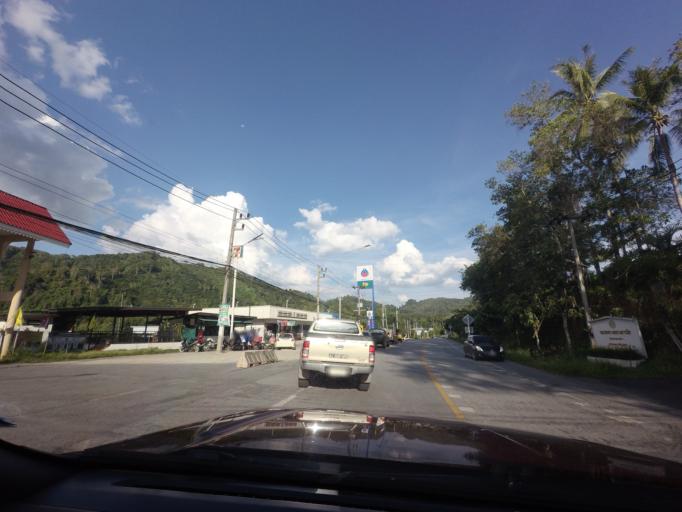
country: TH
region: Yala
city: Than To
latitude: 6.1607
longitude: 101.1878
